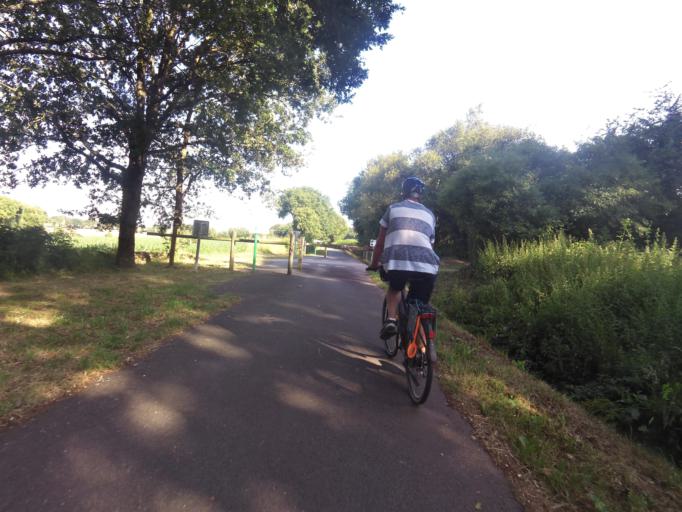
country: FR
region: Brittany
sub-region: Departement du Morbihan
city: Malestroit
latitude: 47.8197
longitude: -2.4178
